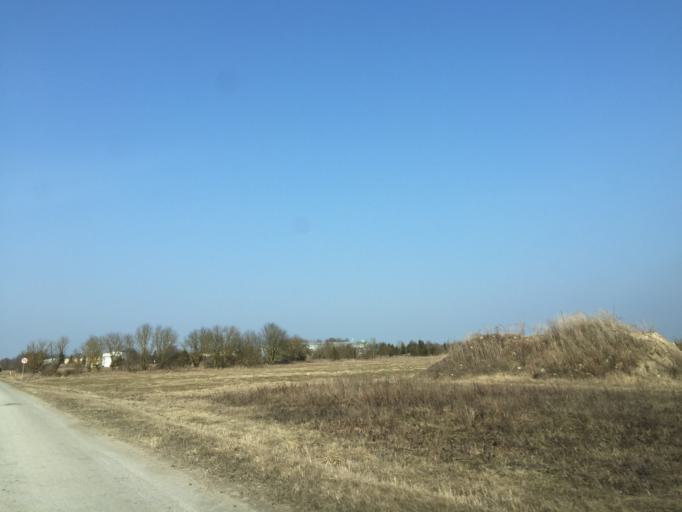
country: EE
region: Saare
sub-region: Orissaare vald
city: Orissaare
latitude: 58.4972
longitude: 23.1156
